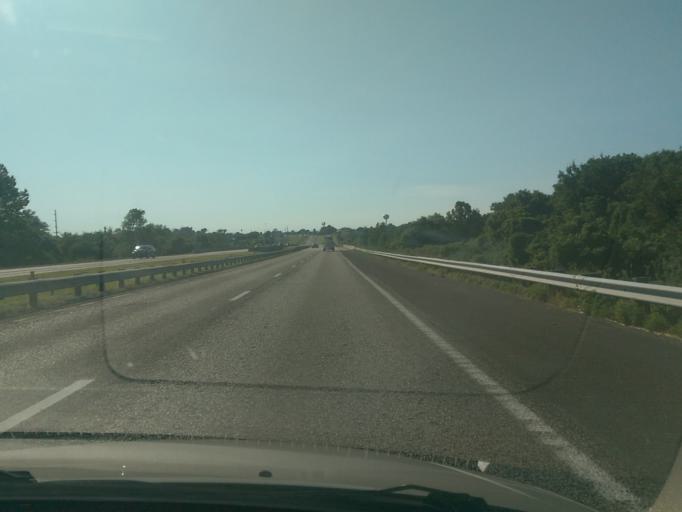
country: US
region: Missouri
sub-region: Lafayette County
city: Higginsville
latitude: 38.9953
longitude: -93.7155
